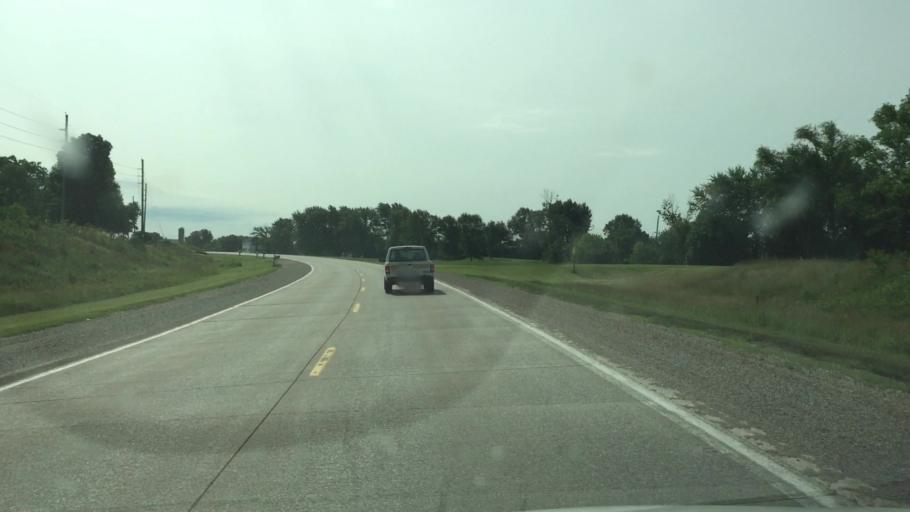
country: US
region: Illinois
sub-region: Hancock County
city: Nauvoo
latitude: 40.6326
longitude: -91.5132
